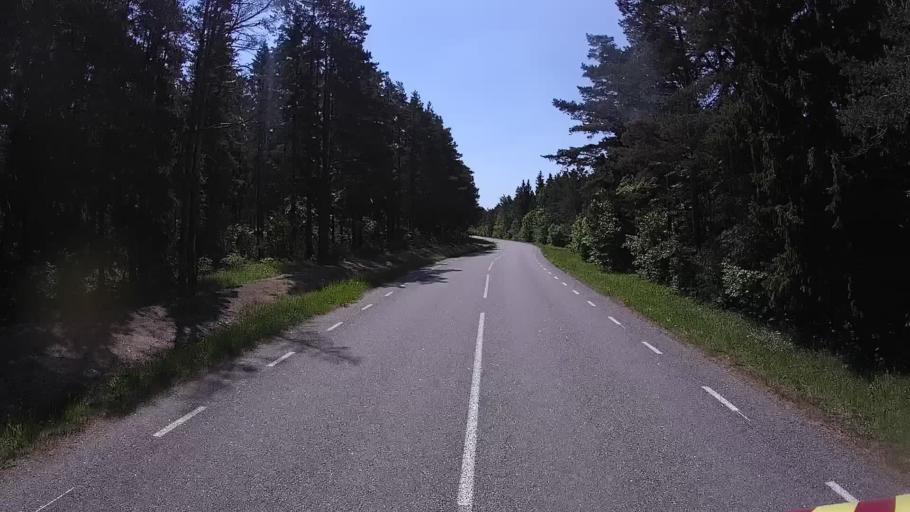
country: EE
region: Saare
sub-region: Kuressaare linn
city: Kuressaare
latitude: 58.0131
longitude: 22.1676
